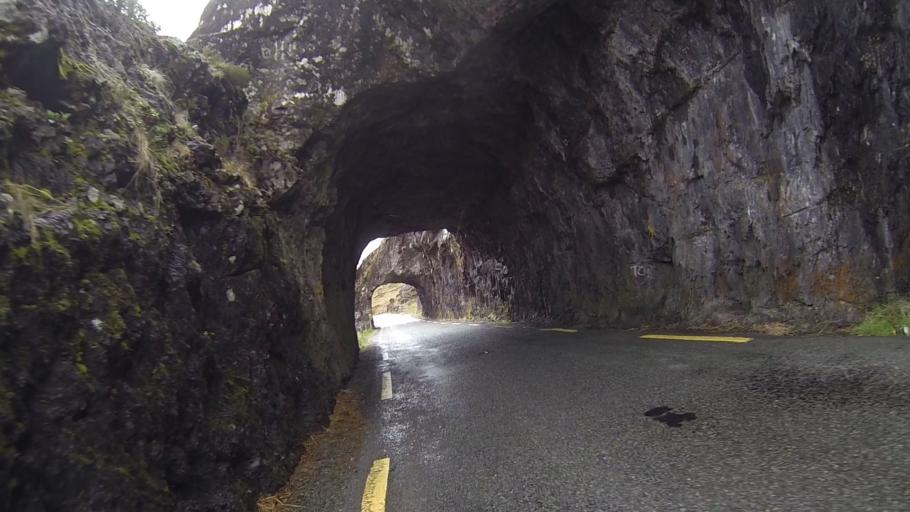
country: IE
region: Munster
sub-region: Ciarrai
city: Kenmare
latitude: 51.7899
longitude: -9.5932
